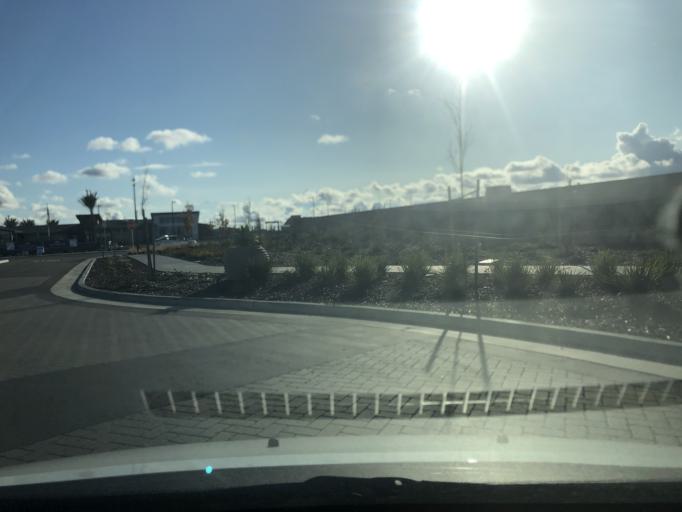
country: US
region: California
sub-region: Sacramento County
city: Antelope
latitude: 38.7748
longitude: -121.3924
